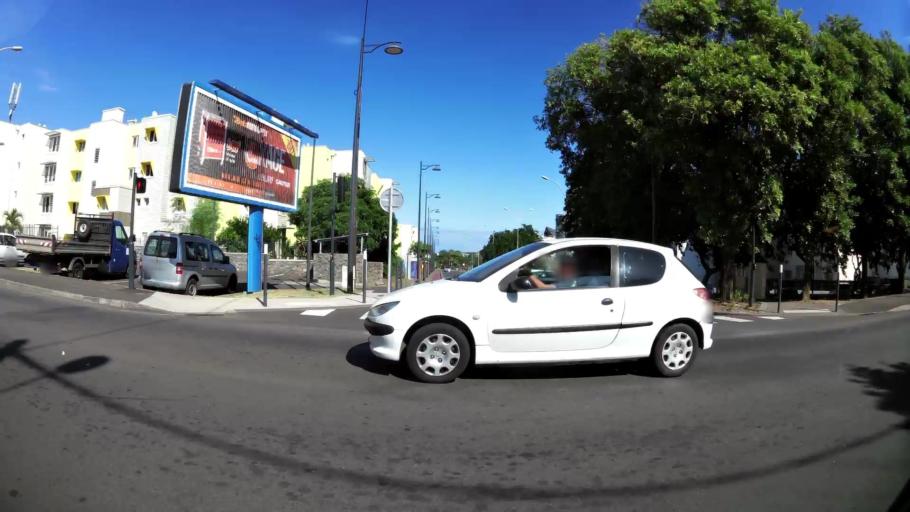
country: RE
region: Reunion
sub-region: Reunion
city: Saint-Pierre
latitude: -21.3349
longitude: 55.4641
